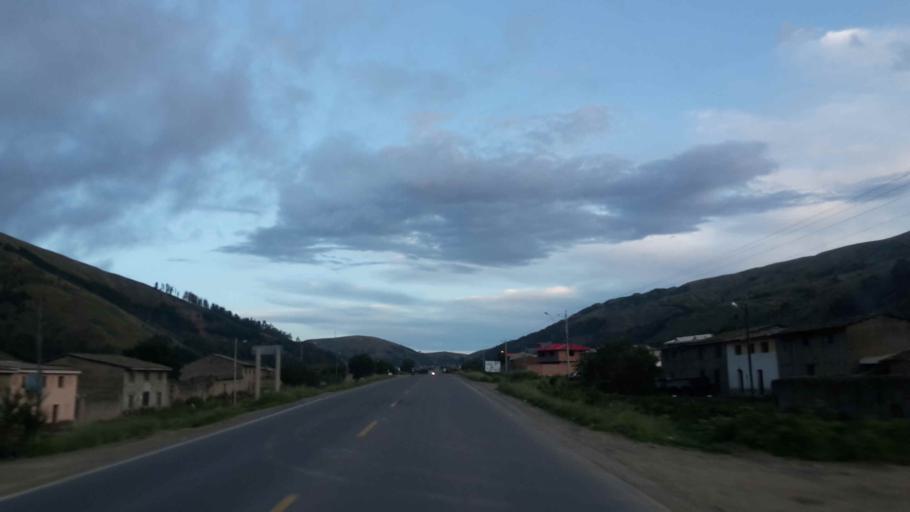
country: BO
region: Cochabamba
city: Colomi
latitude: -17.3417
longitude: -65.8616
